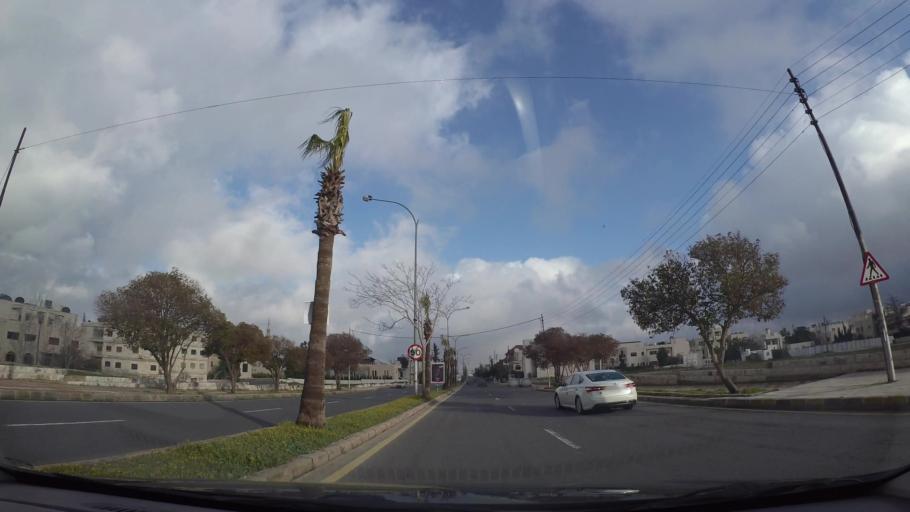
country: JO
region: Amman
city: Wadi as Sir
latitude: 31.9538
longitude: 35.8780
